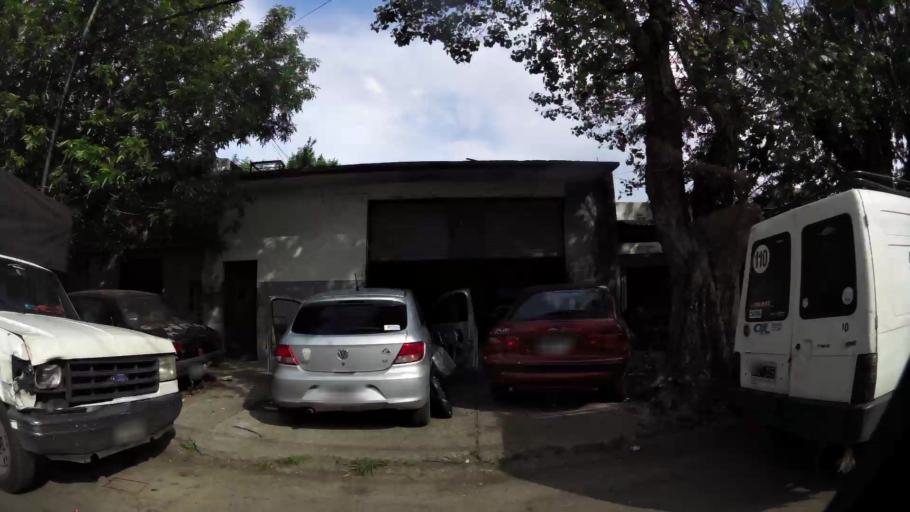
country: AR
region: Buenos Aires
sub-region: Partido de Lanus
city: Lanus
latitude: -34.6914
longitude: -58.3809
